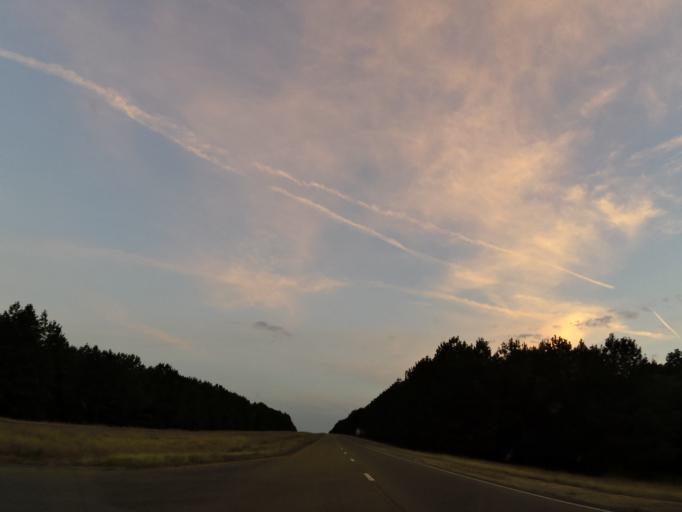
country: US
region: Mississippi
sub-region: Lauderdale County
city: Meridian Station
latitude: 32.6407
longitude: -88.4962
